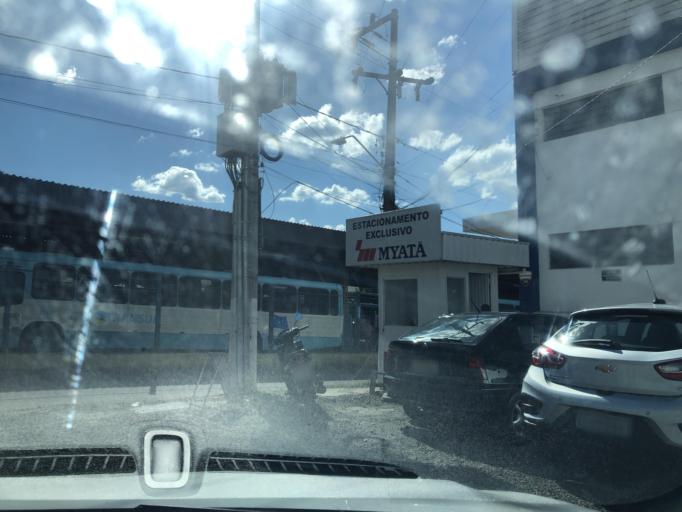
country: BR
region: Santa Catarina
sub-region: Lages
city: Lages
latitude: -27.8129
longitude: -50.3277
